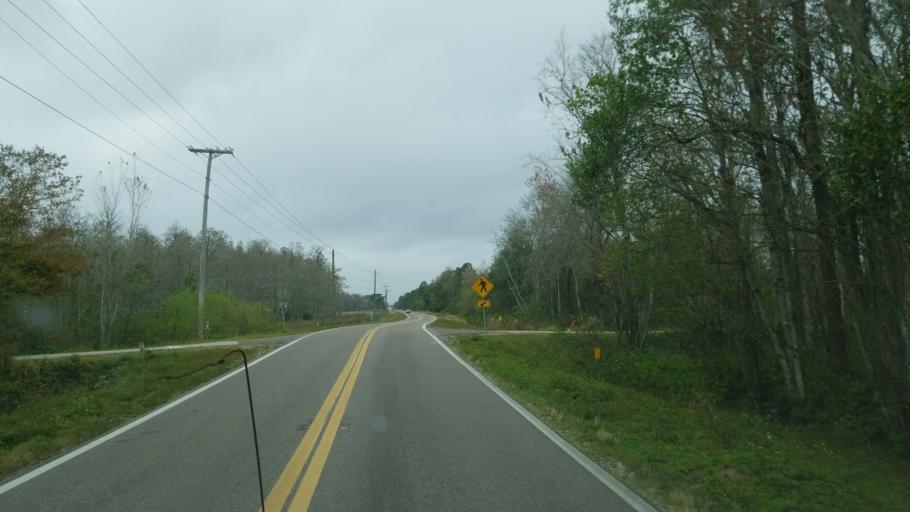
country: US
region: Florida
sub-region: Polk County
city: Polk City
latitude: 28.2585
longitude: -81.8353
